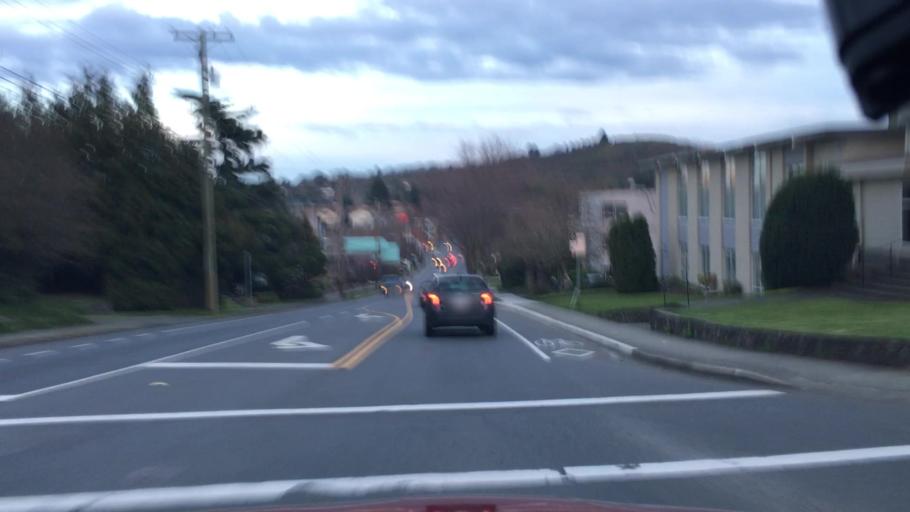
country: CA
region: British Columbia
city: Oak Bay
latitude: 48.4627
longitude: -123.3369
